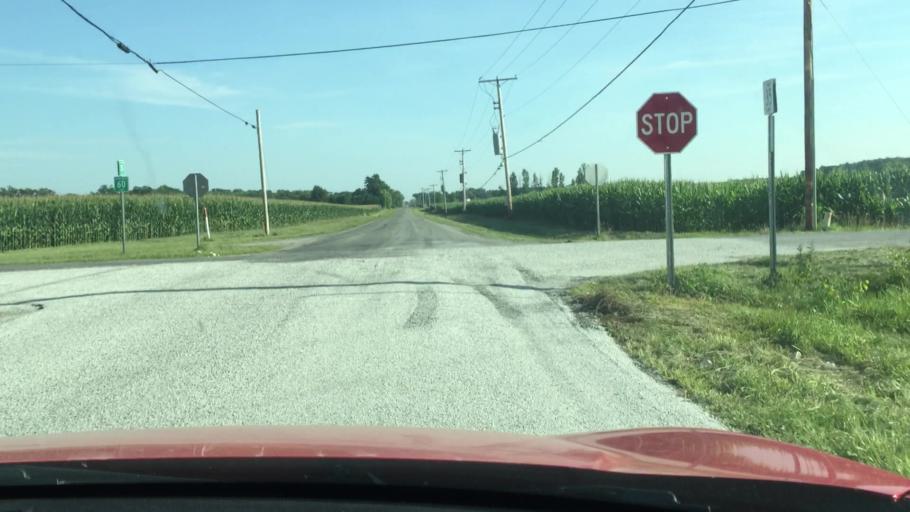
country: US
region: Ohio
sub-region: Hardin County
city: Ada
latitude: 40.7476
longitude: -83.8424
